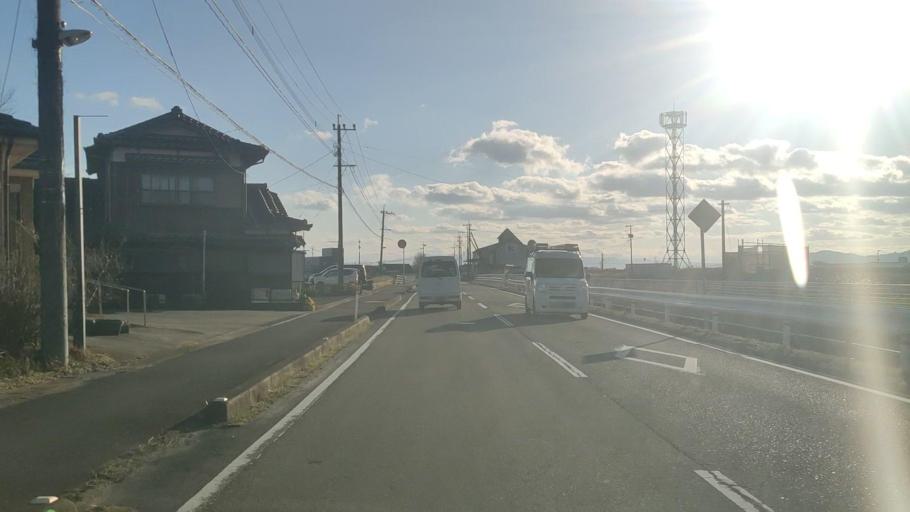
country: JP
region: Saga Prefecture
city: Saga-shi
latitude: 33.2873
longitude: 130.2334
